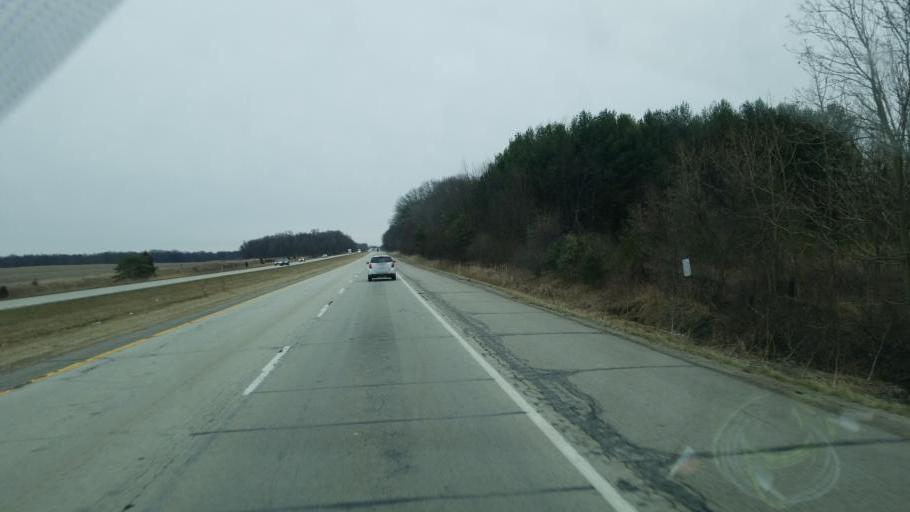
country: US
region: Indiana
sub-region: Starke County
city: Koontz Lake
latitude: 41.3644
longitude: -86.4254
